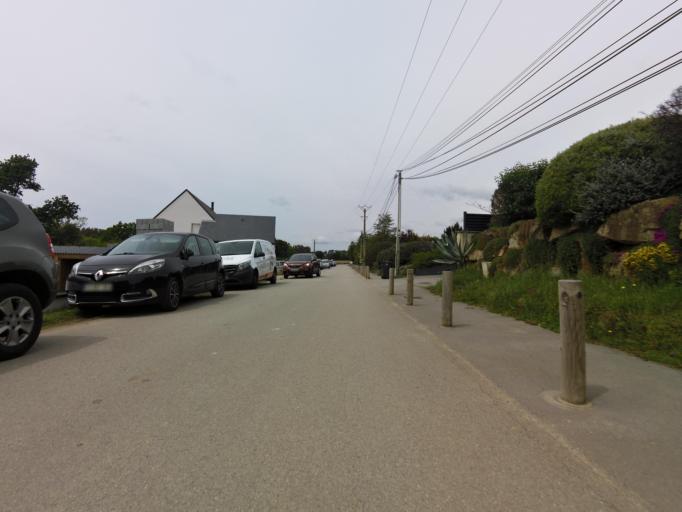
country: FR
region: Brittany
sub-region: Departement du Morbihan
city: Larmor-Baden
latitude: 47.6025
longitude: -2.8685
